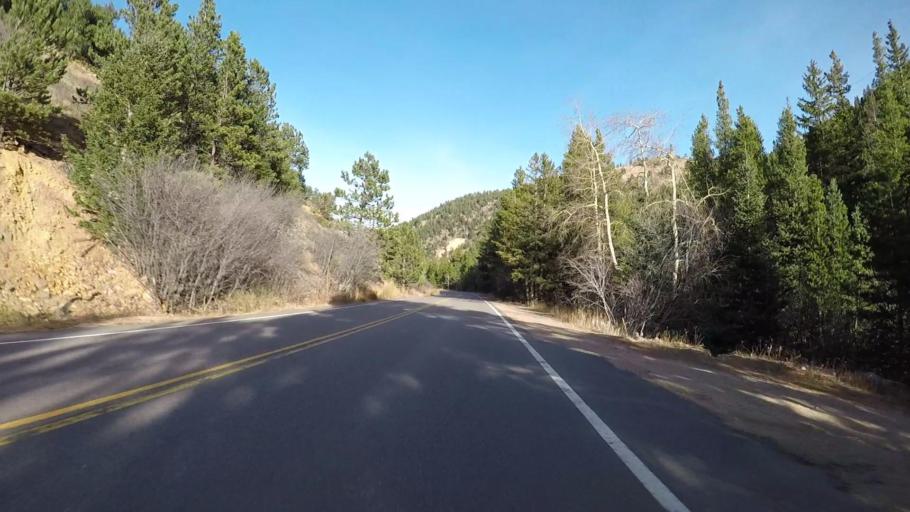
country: US
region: Colorado
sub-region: Boulder County
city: Nederland
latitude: 40.0559
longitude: -105.4956
